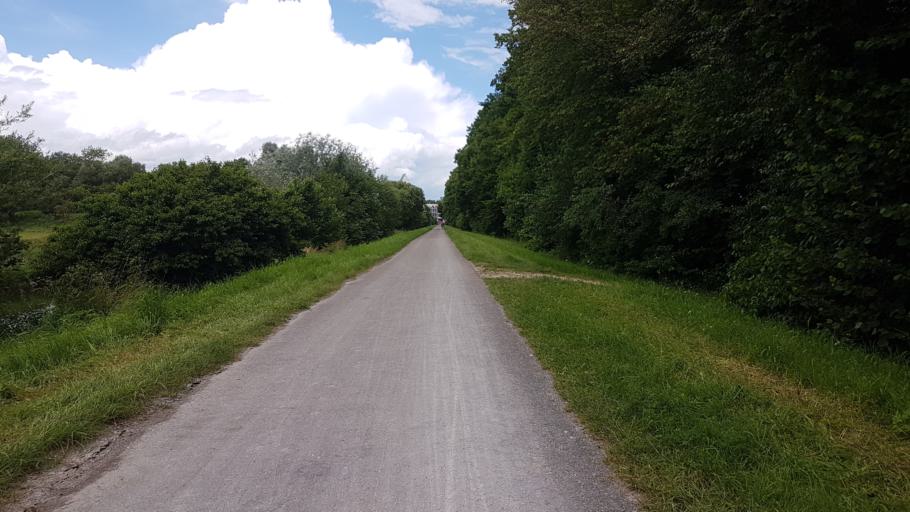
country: DE
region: Baden-Wuerttemberg
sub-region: Tuebingen Region
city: Riedlingen
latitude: 48.1473
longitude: 9.4764
